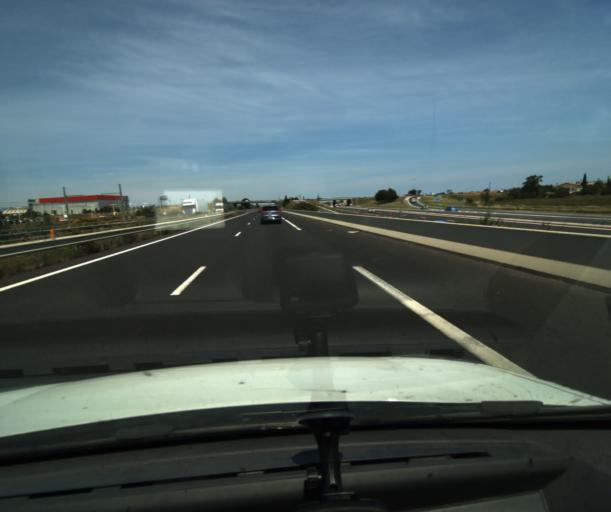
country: FR
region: Languedoc-Roussillon
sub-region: Departement des Pyrenees-Orientales
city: Perpignan
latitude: 42.7250
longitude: 2.8769
